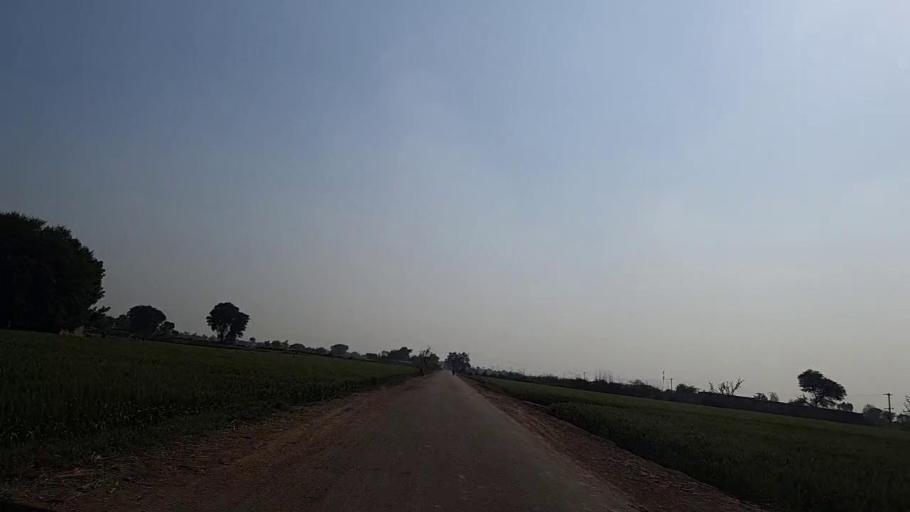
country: PK
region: Sindh
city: Sakrand
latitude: 26.0837
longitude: 68.2901
